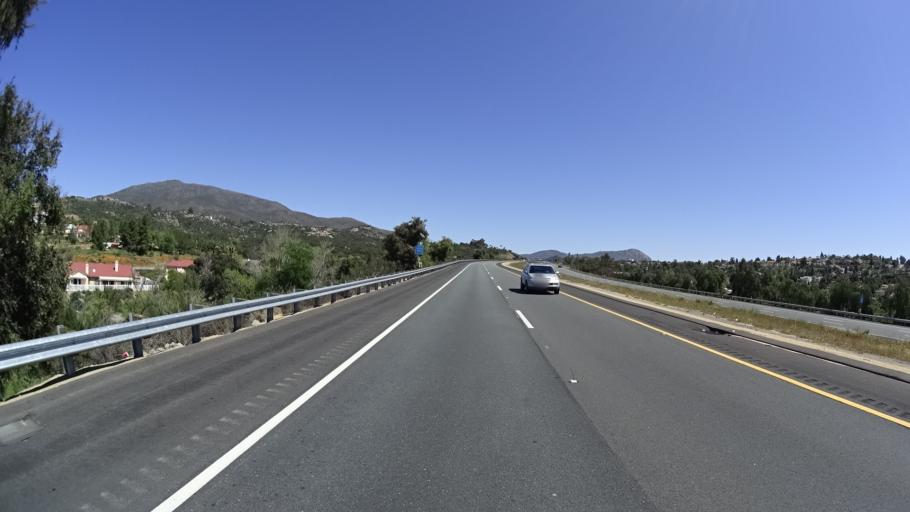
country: US
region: California
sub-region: San Diego County
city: Alpine
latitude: 32.8385
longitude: -116.7629
